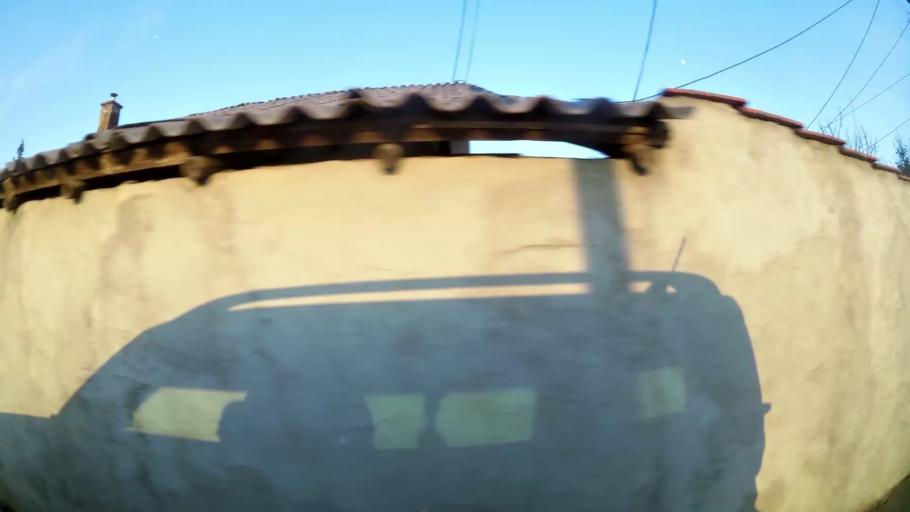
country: MK
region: Kisela Voda
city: Kisela Voda
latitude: 41.9795
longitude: 21.4950
